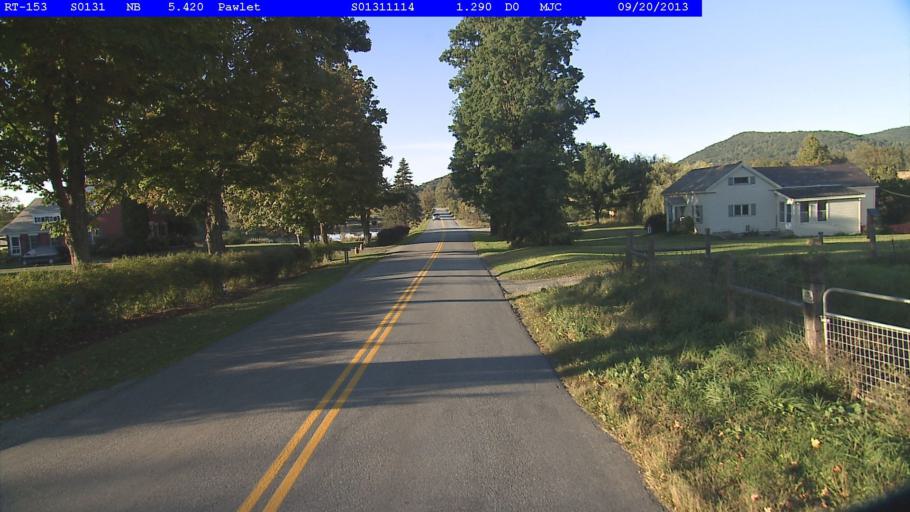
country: US
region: New York
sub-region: Washington County
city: Granville
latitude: 43.3325
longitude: -73.2434
